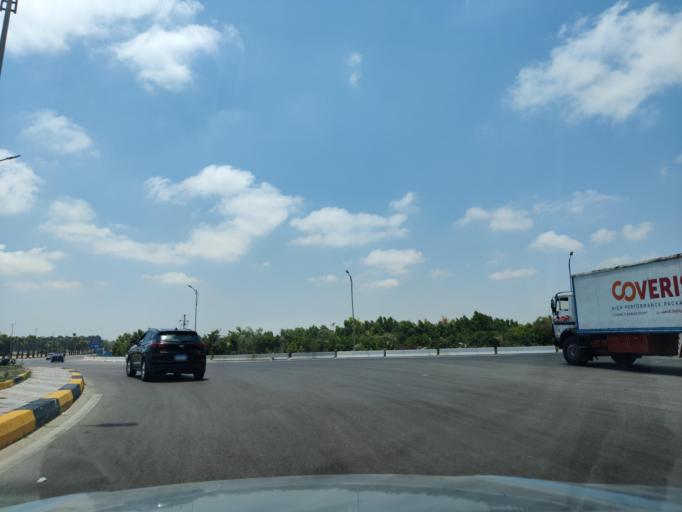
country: EG
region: Alexandria
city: Alexandria
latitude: 30.9756
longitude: 29.6611
